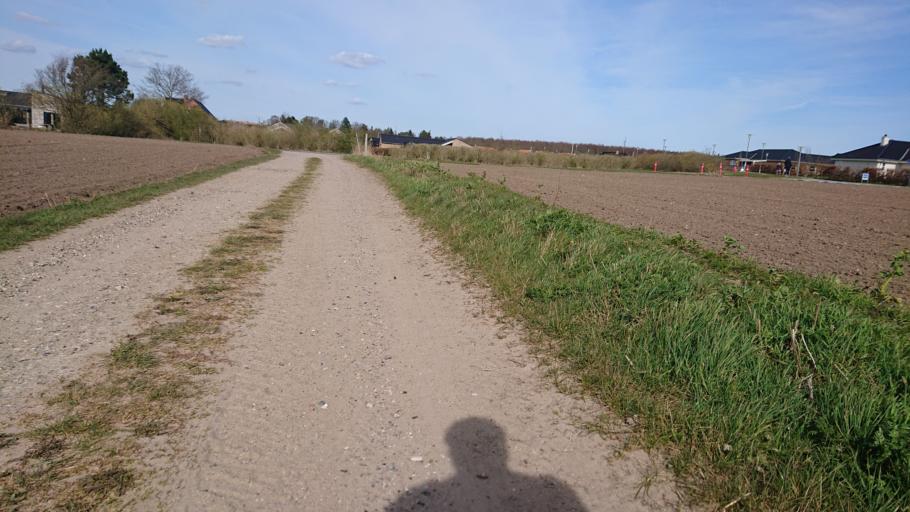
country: DK
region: South Denmark
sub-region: Nyborg Kommune
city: Nyborg
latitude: 55.3056
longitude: 10.7510
